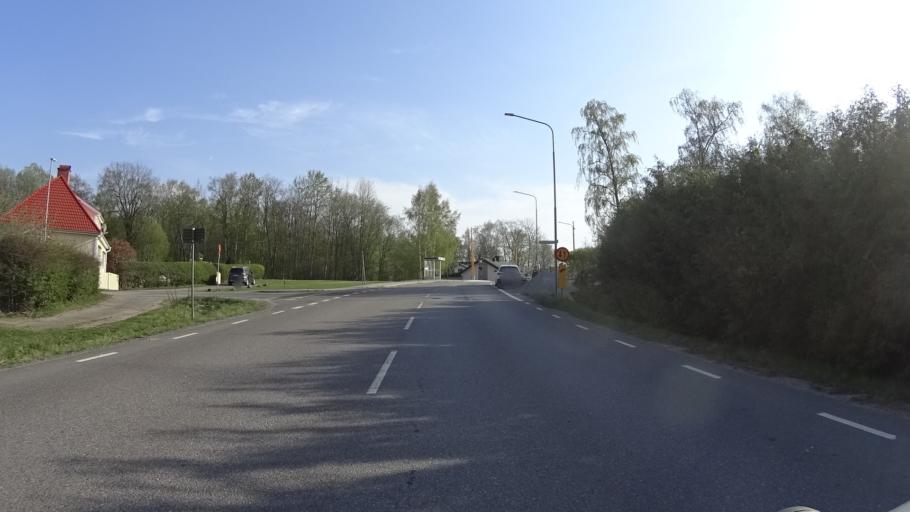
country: SE
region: Vaestra Goetaland
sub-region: Gotene Kommun
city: Goetene
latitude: 58.6308
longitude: 13.4342
